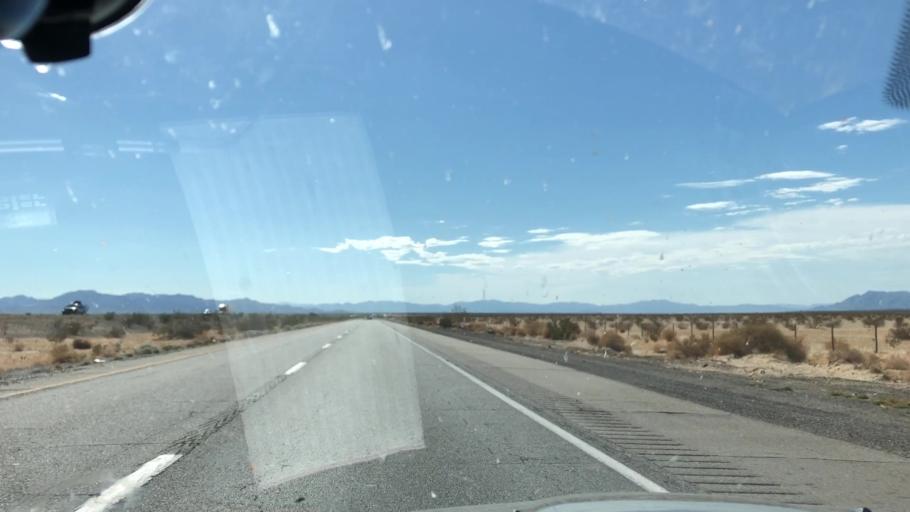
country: US
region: California
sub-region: Riverside County
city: Mesa Verde
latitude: 33.6386
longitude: -115.0911
